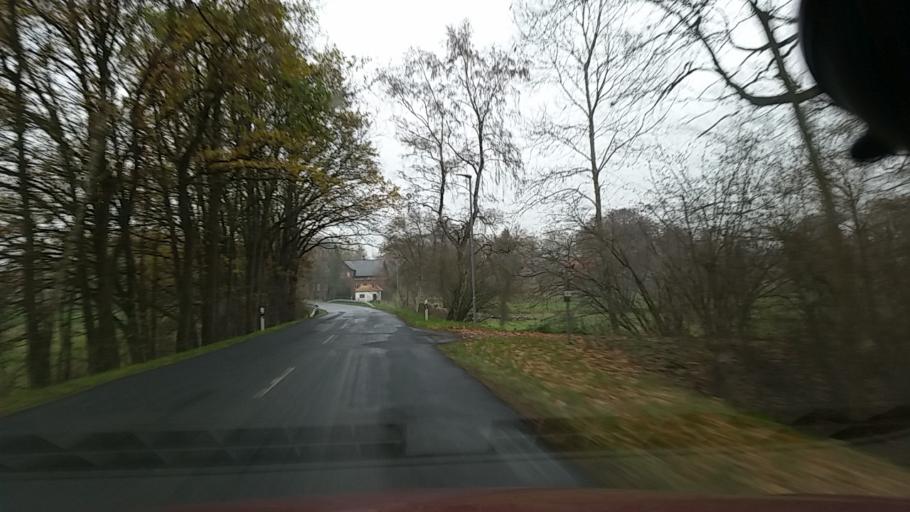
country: DE
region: Lower Saxony
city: Obernholz
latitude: 52.7631
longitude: 10.5976
